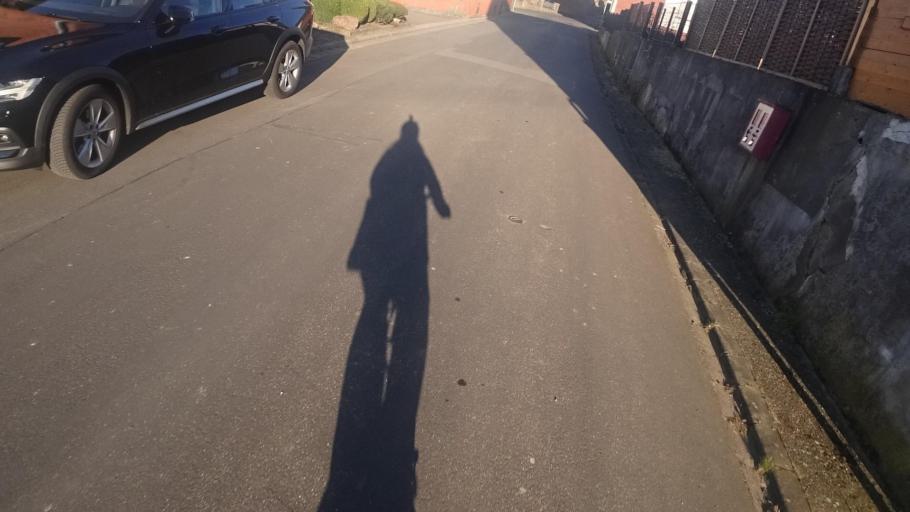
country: DE
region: Rheinland-Pfalz
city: Ney
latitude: 50.2097
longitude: 7.5288
